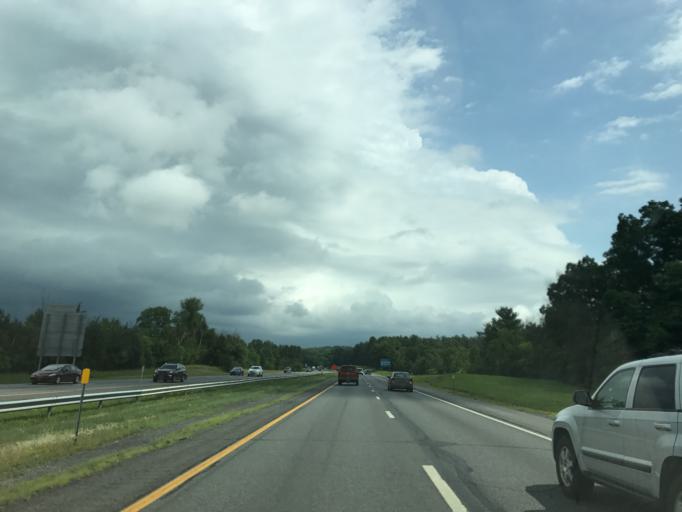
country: US
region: New York
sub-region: Greene County
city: Coxsackie
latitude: 42.4084
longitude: -73.8153
